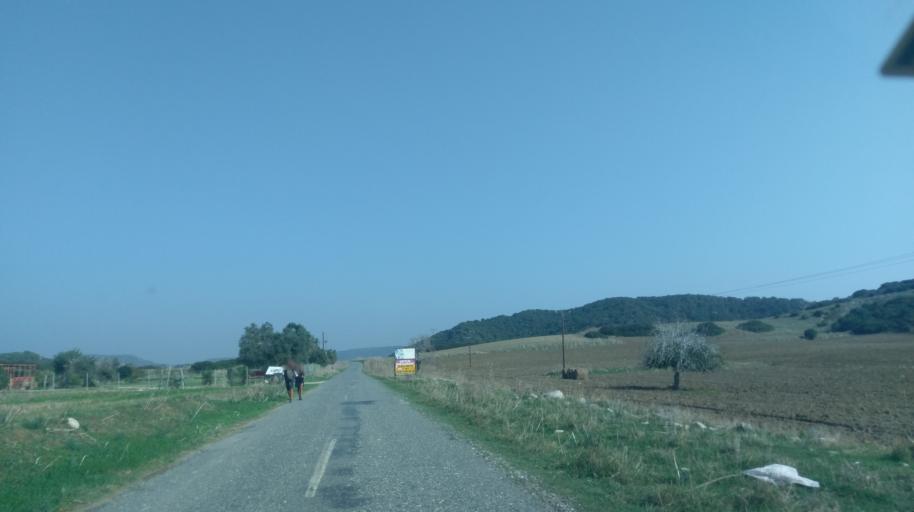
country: CY
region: Ammochostos
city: Rizokarpaso
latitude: 35.6355
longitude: 34.5075
